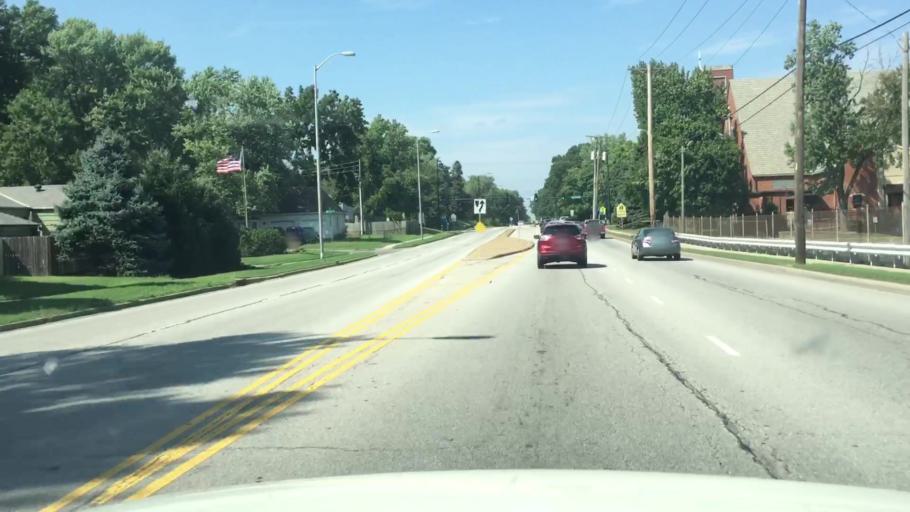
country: US
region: Kansas
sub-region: Johnson County
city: Overland Park
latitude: 38.9989
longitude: -94.6677
